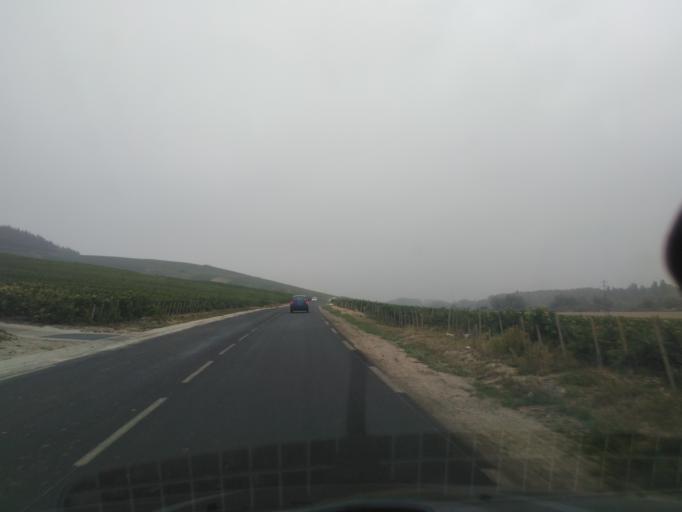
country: FR
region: Champagne-Ardenne
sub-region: Departement de la Marne
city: Damery
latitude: 49.0699
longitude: 3.8978
